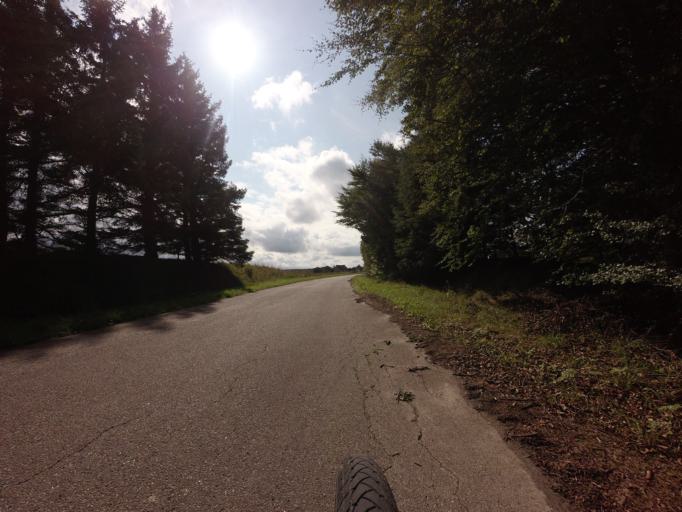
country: DK
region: North Denmark
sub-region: Hjorring Kommune
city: Hjorring
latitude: 57.5378
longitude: 10.0571
